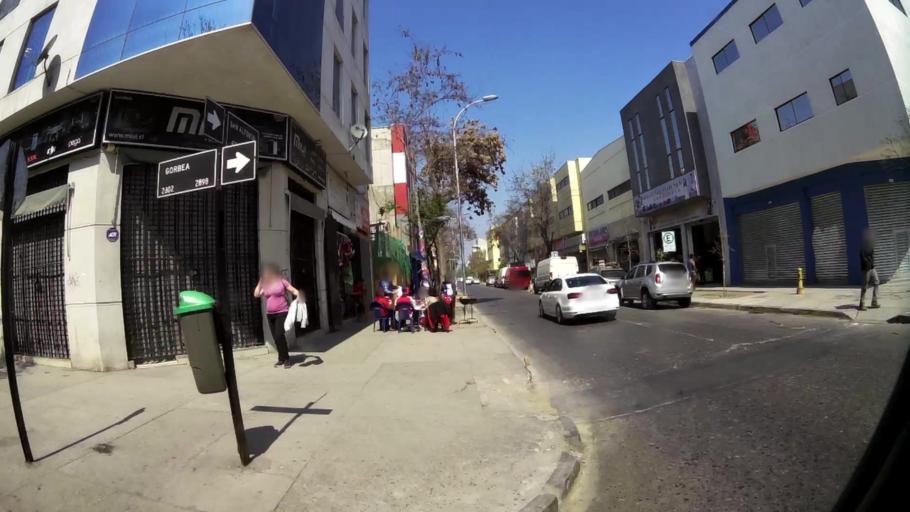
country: CL
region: Santiago Metropolitan
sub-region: Provincia de Santiago
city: Santiago
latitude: -33.4552
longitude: -70.6757
